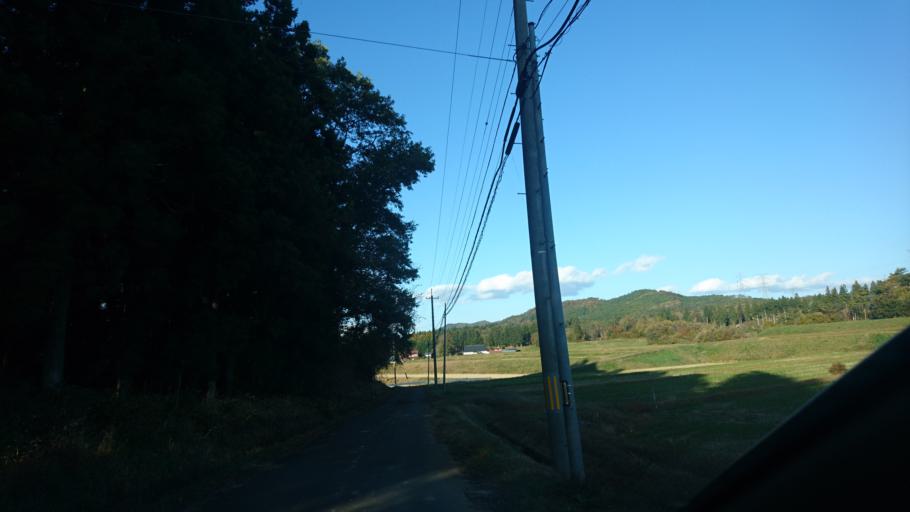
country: JP
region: Iwate
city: Ichinoseki
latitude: 38.9137
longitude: 141.2076
